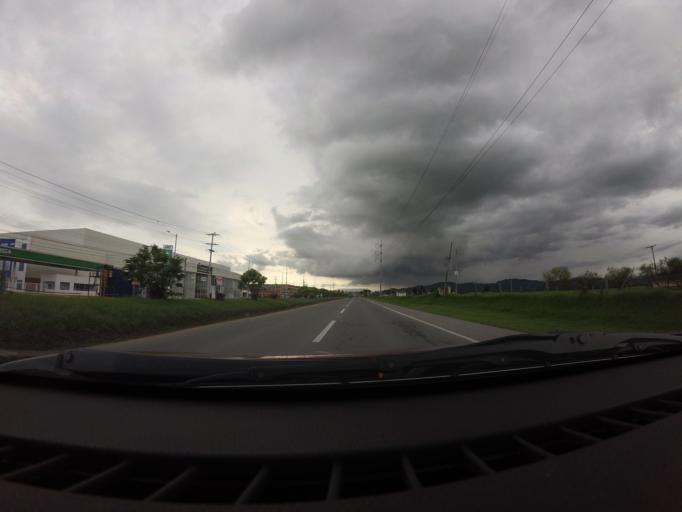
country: CO
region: Cundinamarca
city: Funza
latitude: 4.7751
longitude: -74.1779
